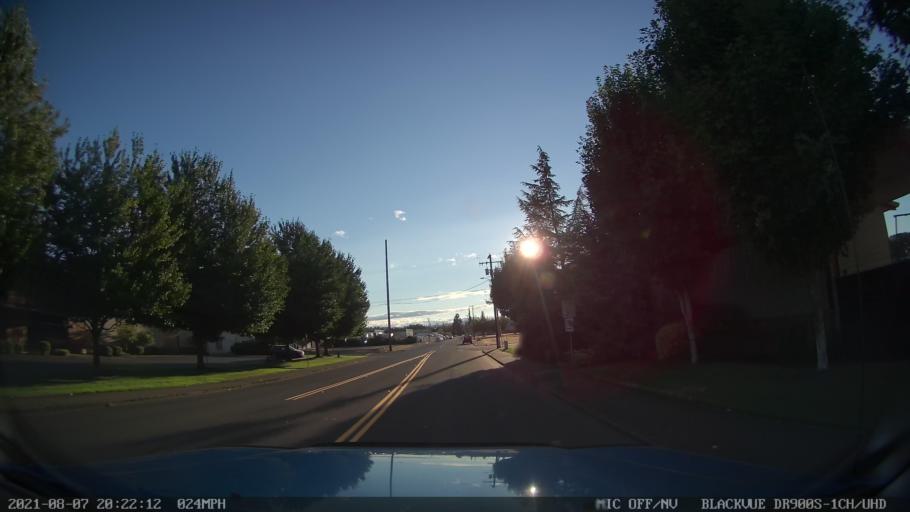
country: US
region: Oregon
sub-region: Marion County
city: Salem
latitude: 44.9563
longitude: -123.0113
